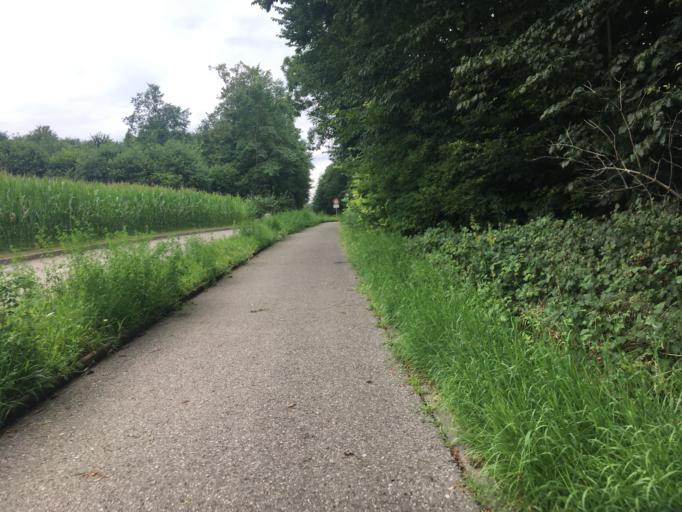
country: CH
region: Fribourg
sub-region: See District
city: Gurwolf
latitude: 46.9116
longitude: 7.1000
